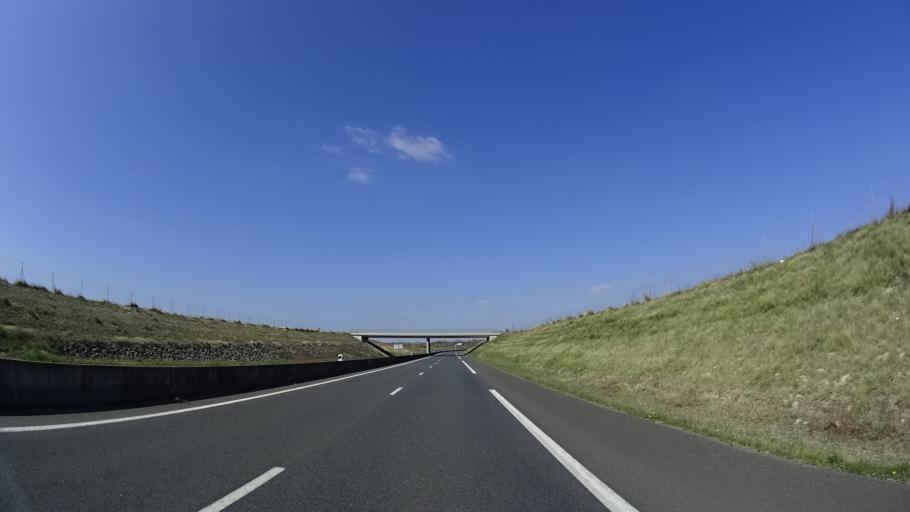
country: FR
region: Pays de la Loire
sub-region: Departement de Maine-et-Loire
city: Saint-Jean
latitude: 47.2898
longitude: -0.3817
